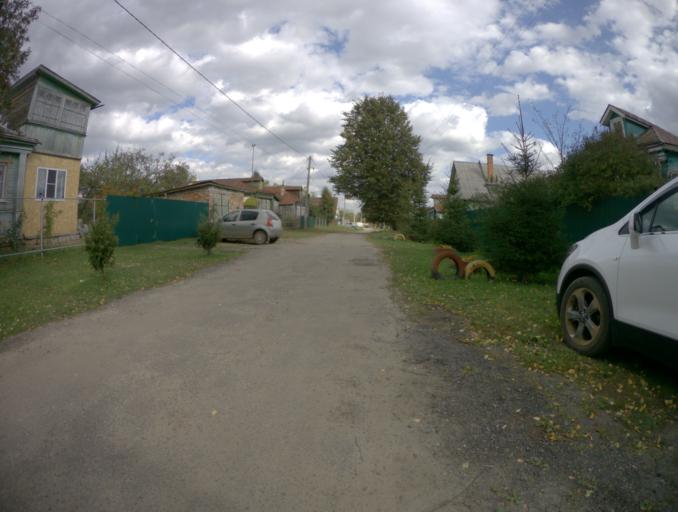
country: RU
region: Vladimir
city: Lakinsk
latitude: 56.0070
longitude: 39.9698
